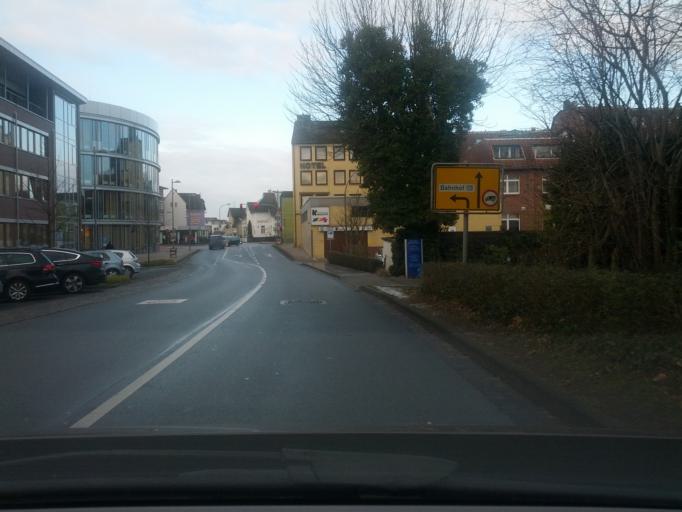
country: DE
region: Lower Saxony
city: Buxtehude
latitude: 53.4738
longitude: 9.6970
